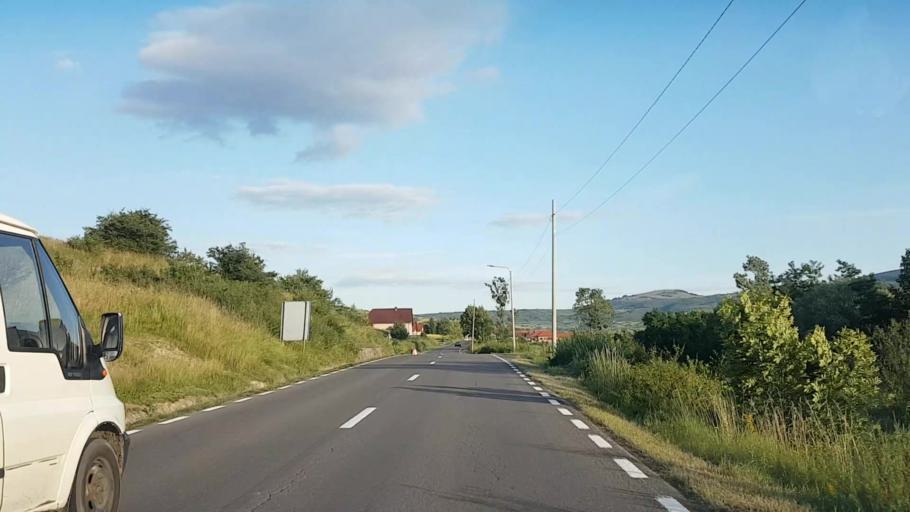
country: RO
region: Harghita
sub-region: Comuna Praid
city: Ocna de Sus
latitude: 46.4985
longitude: 25.1656
